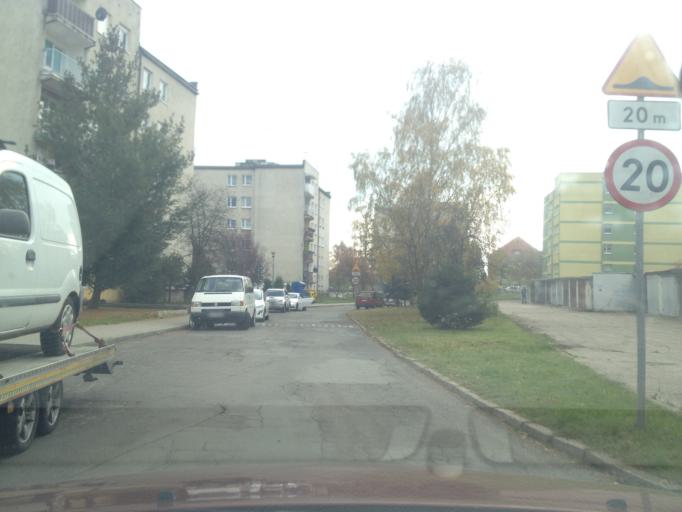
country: PL
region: Lower Silesian Voivodeship
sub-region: Powiat zgorzelecki
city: Zgorzelec
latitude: 51.1503
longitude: 15.0146
